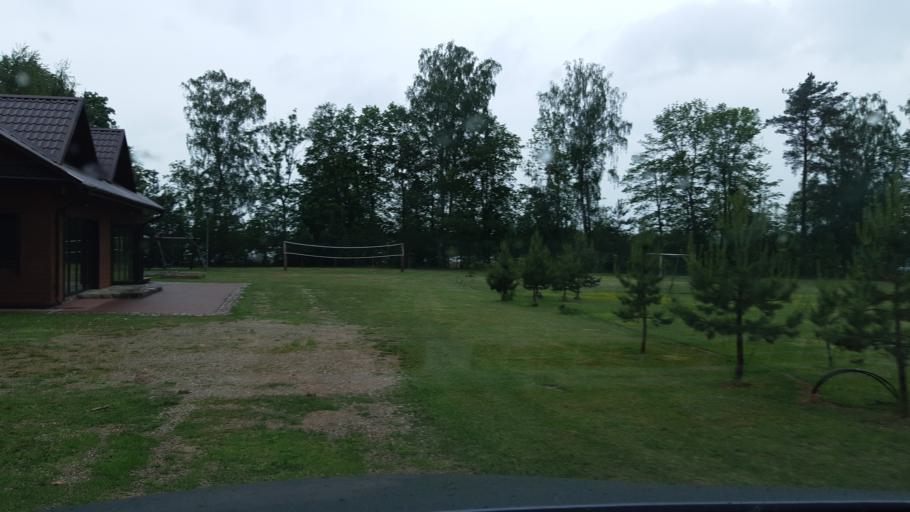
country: LT
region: Utenos apskritis
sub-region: Anyksciai
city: Anyksciai
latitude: 55.4462
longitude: 25.1902
